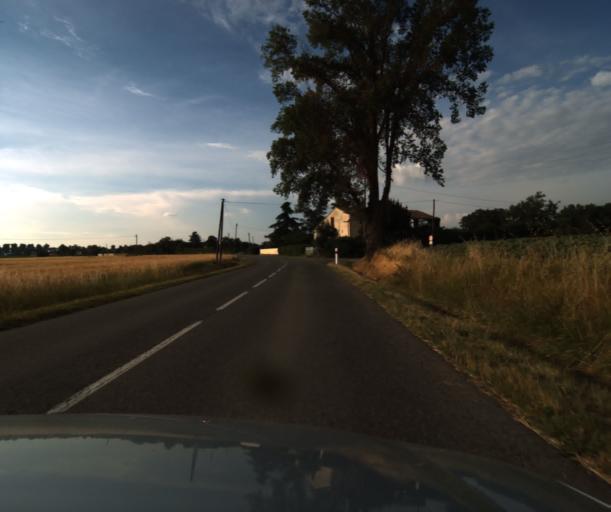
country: FR
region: Midi-Pyrenees
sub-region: Departement du Tarn-et-Garonne
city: Castelsarrasin
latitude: 44.0262
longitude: 1.1101
